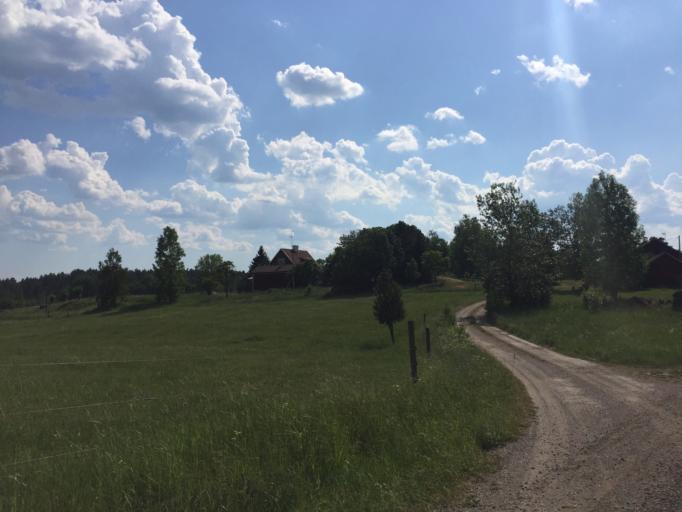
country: SE
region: Soedermanland
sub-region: Flens Kommun
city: Halleforsnas
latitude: 59.0750
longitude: 16.4645
